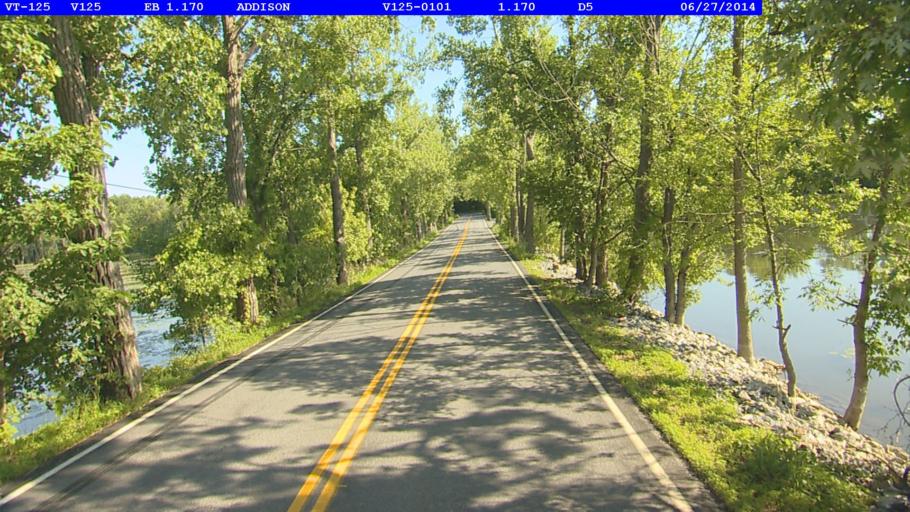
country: US
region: New York
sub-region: Essex County
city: Port Henry
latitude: 44.0281
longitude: -73.3991
